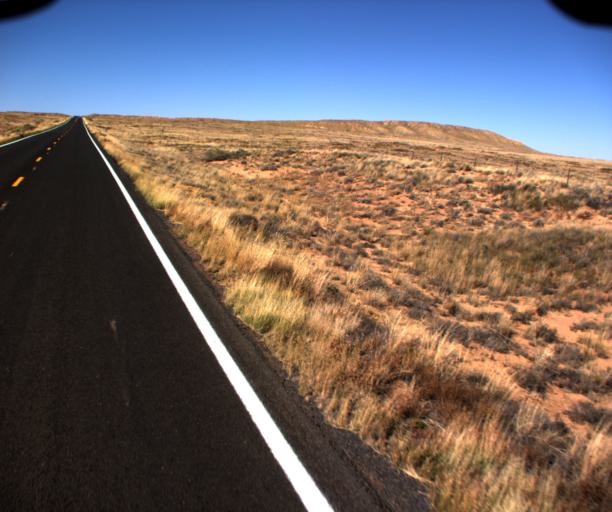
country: US
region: Arizona
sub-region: Coconino County
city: Tuba City
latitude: 35.9518
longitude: -110.9240
